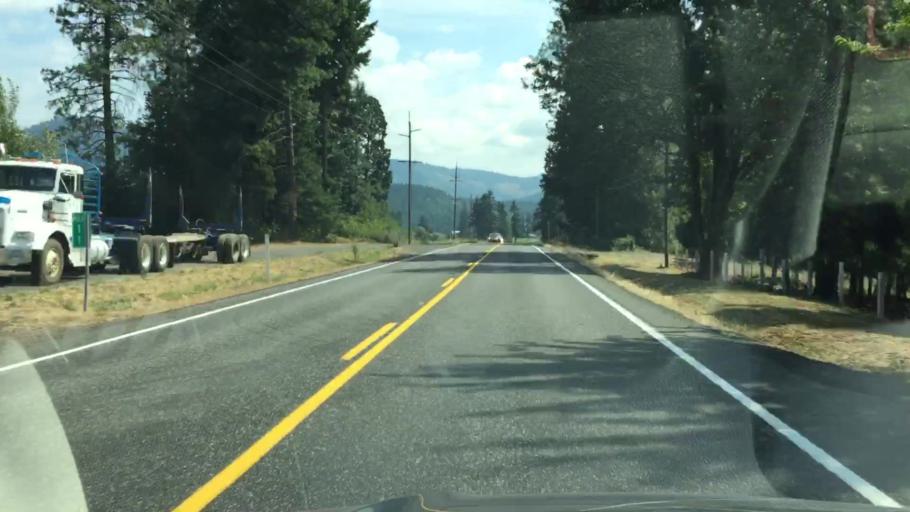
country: US
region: Washington
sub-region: Klickitat County
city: White Salmon
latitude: 45.8304
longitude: -121.4939
